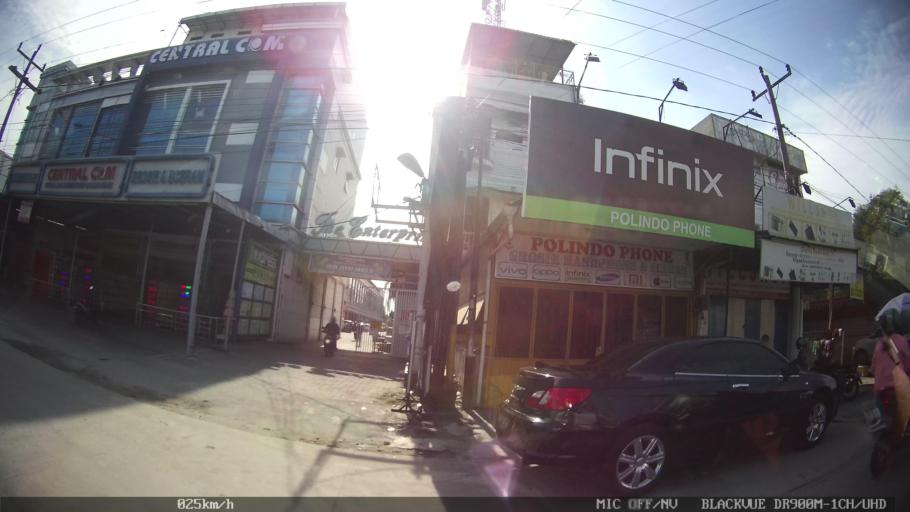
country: ID
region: North Sumatra
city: Medan
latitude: 3.6000
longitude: 98.6451
